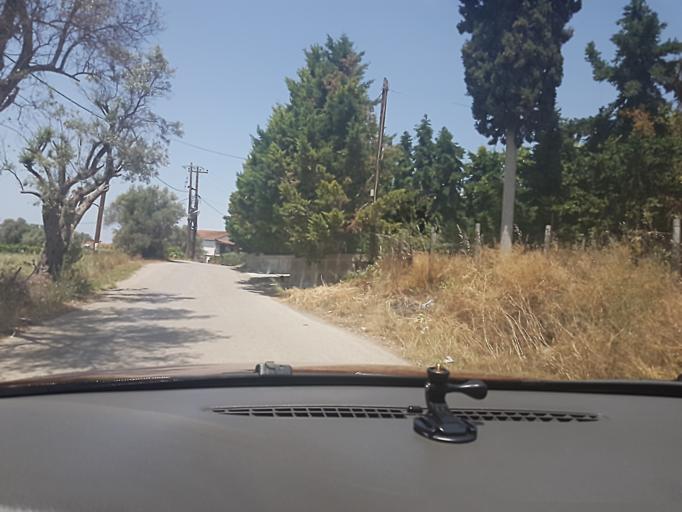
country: GR
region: Central Greece
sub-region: Nomos Evvoias
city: Vasilikon
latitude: 38.4183
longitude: 23.6678
